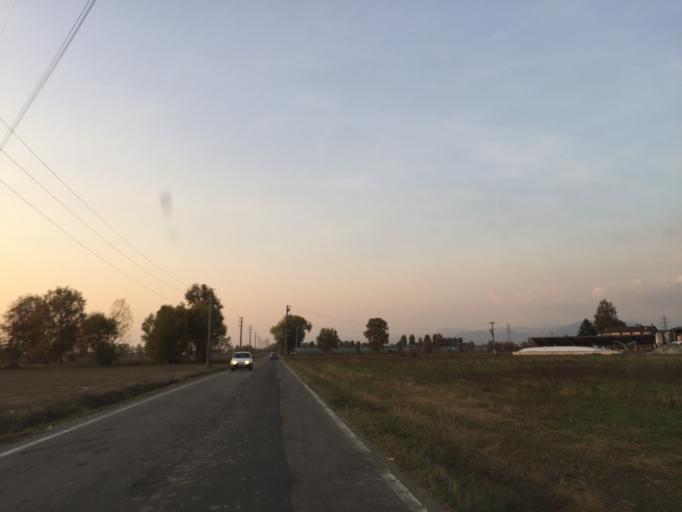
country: IT
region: Lombardy
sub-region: Provincia di Brescia
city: Folzano
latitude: 45.4947
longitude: 10.1914
